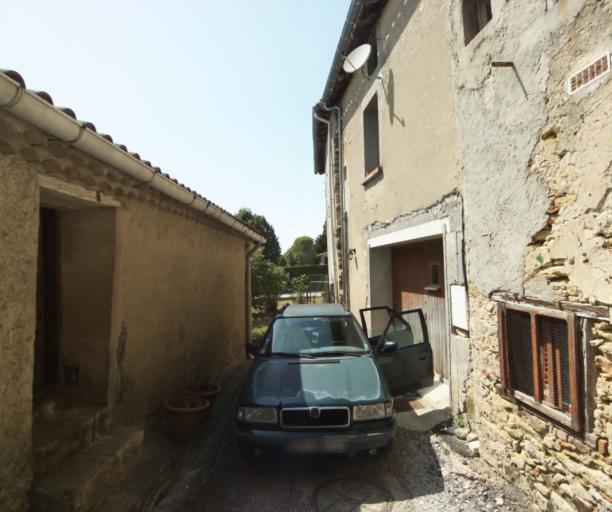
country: FR
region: Midi-Pyrenees
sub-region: Departement de la Haute-Garonne
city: Saint-Felix-Lauragais
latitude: 43.4497
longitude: 1.8846
